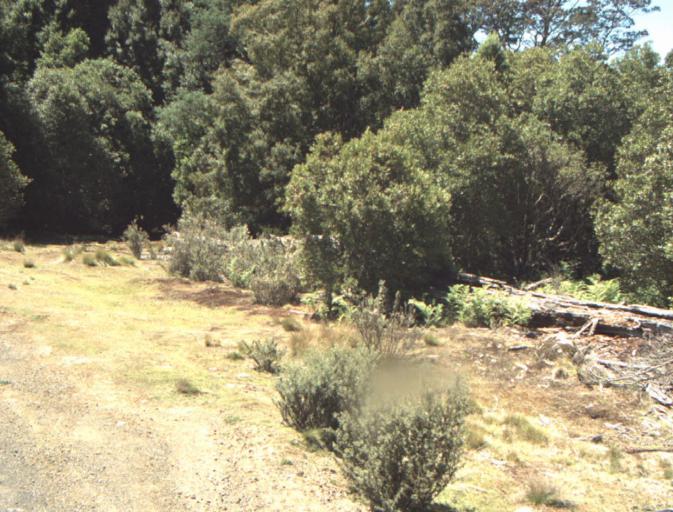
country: AU
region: Tasmania
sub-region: Dorset
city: Scottsdale
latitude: -41.3666
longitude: 147.4301
